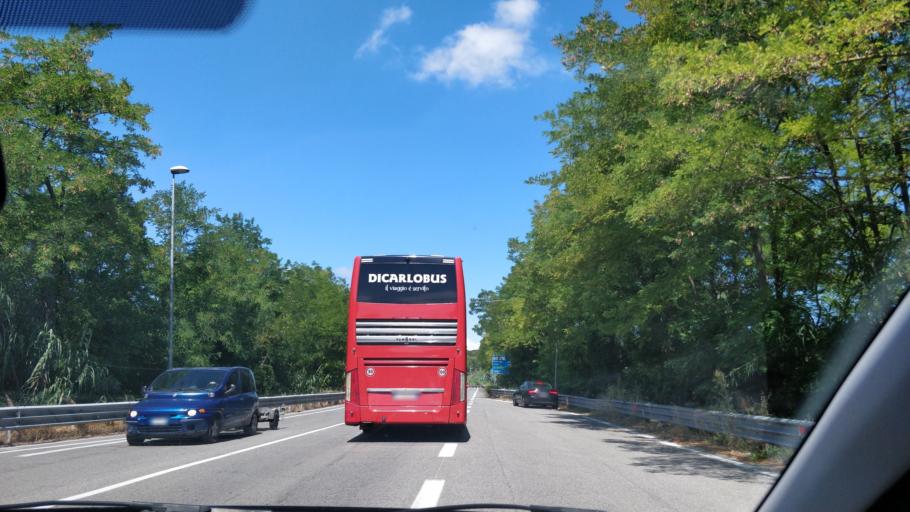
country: IT
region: Abruzzo
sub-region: Provincia di Chieti
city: Francavilla al Mare
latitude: 42.4064
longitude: 14.3010
